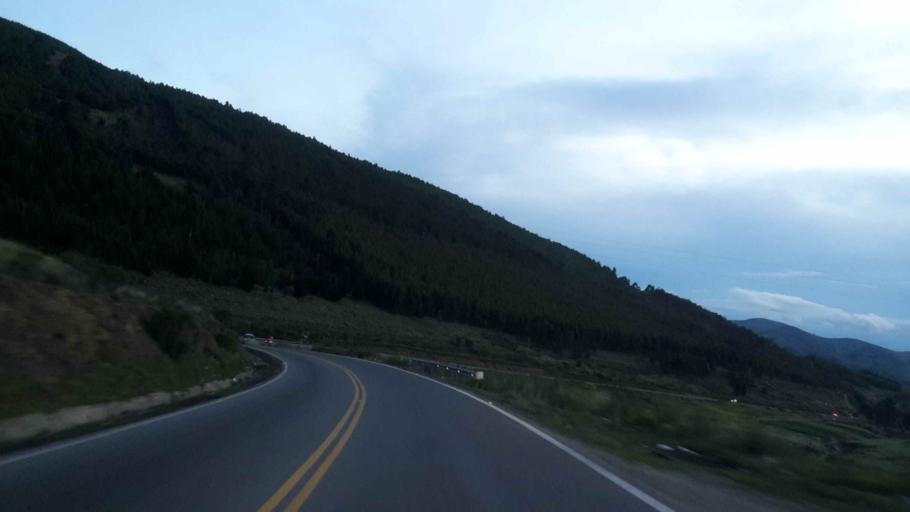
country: BO
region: Cochabamba
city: Colomi
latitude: -17.4035
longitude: -65.8796
